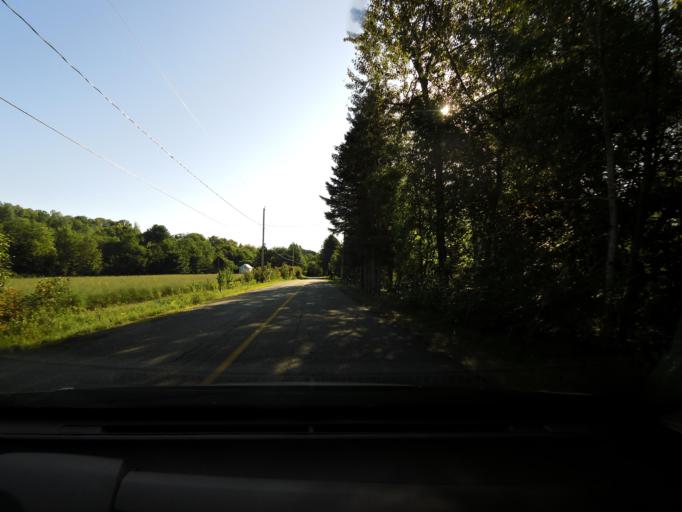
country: CA
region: Quebec
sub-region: Mauricie
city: Becancour
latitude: 46.5531
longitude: -72.3714
